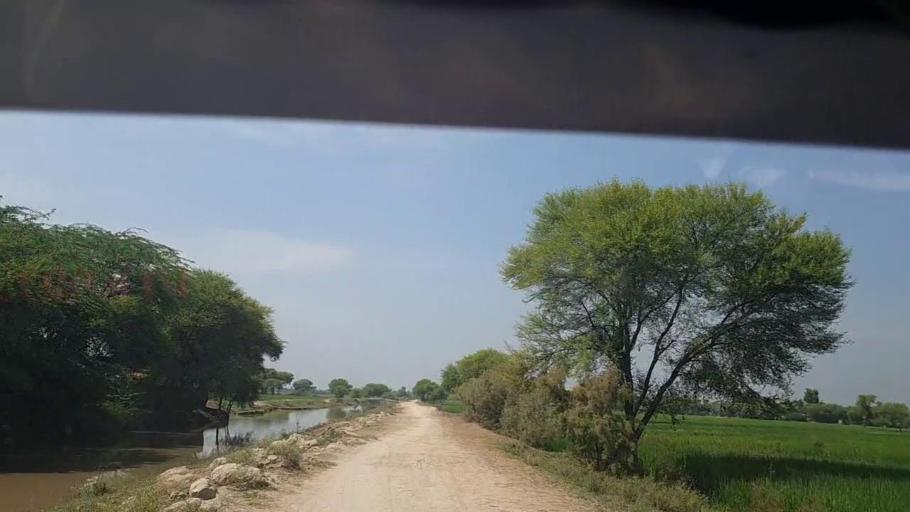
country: PK
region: Sindh
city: Thul
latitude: 28.1979
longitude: 68.7041
